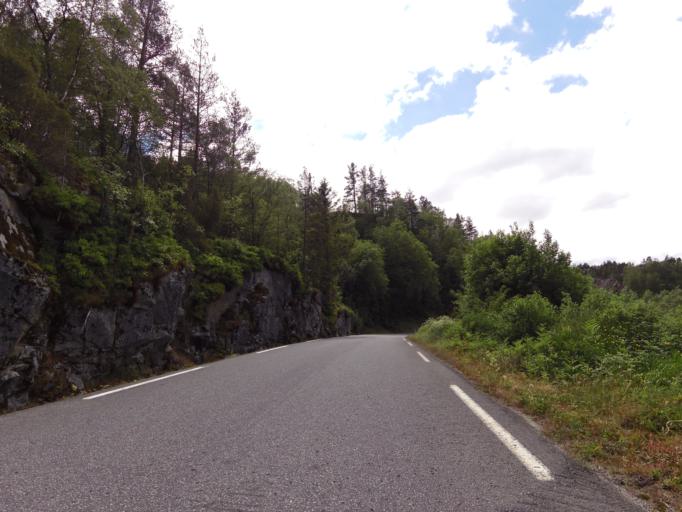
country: NO
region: Vest-Agder
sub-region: Kvinesdal
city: Liknes
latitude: 58.2836
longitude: 6.9286
